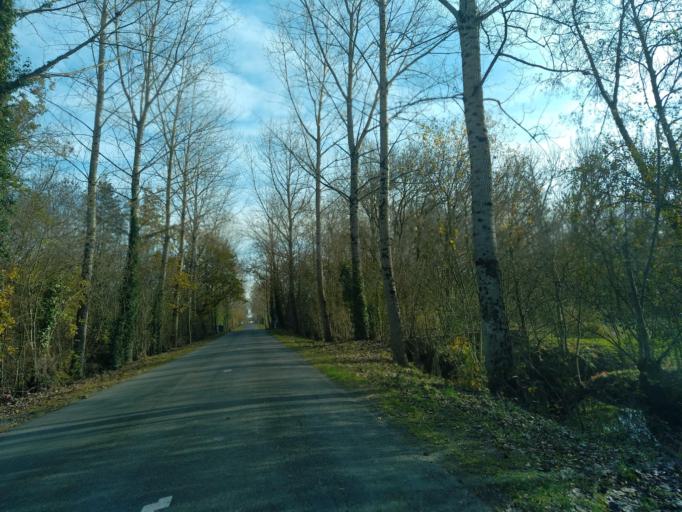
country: FR
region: Pays de la Loire
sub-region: Departement de la Vendee
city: Maillezais
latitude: 46.3771
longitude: -0.7549
